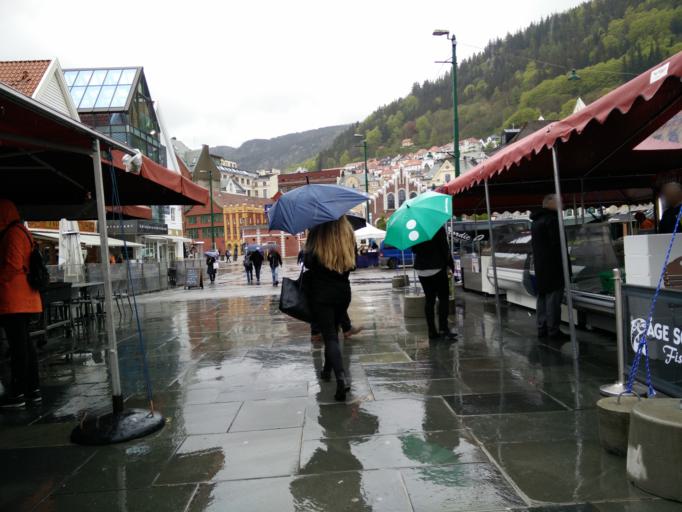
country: NO
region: Hordaland
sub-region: Bergen
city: Bergen
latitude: 60.3949
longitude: 5.3253
